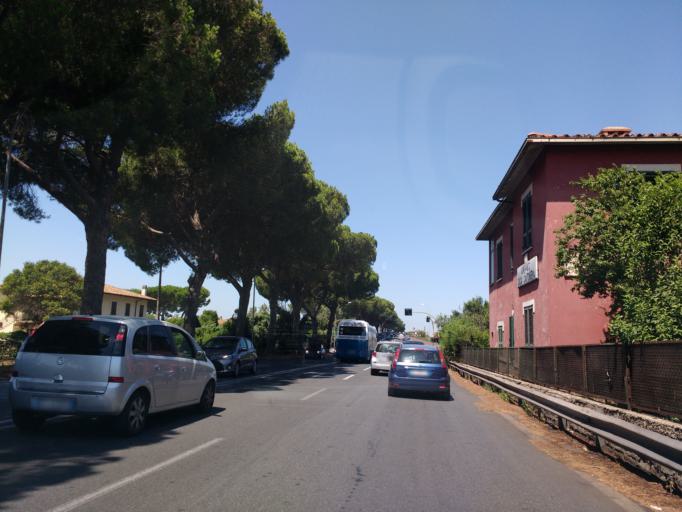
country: IT
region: Latium
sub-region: Citta metropolitana di Roma Capitale
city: Marino
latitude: 41.7748
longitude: 12.6090
